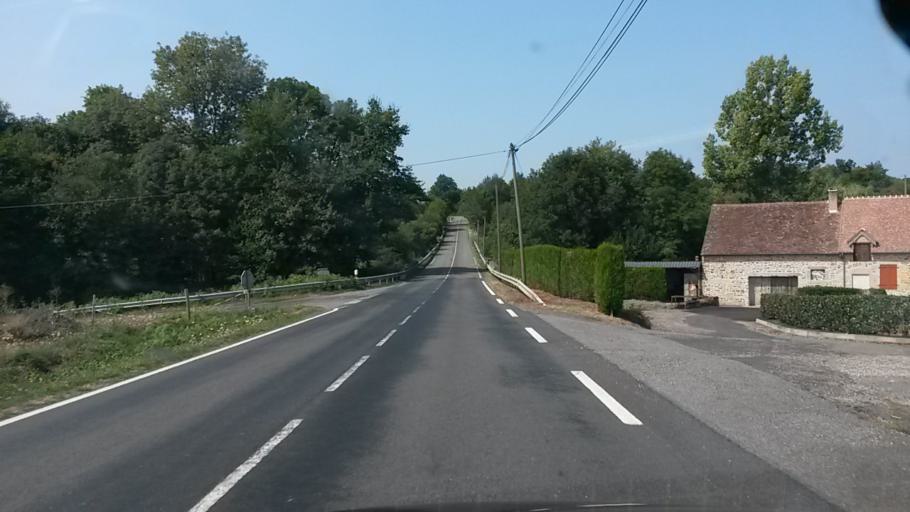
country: FR
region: Lower Normandy
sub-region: Departement de l'Orne
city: Saint-Denis-sur-Sarthon
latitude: 48.4109
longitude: -0.0535
